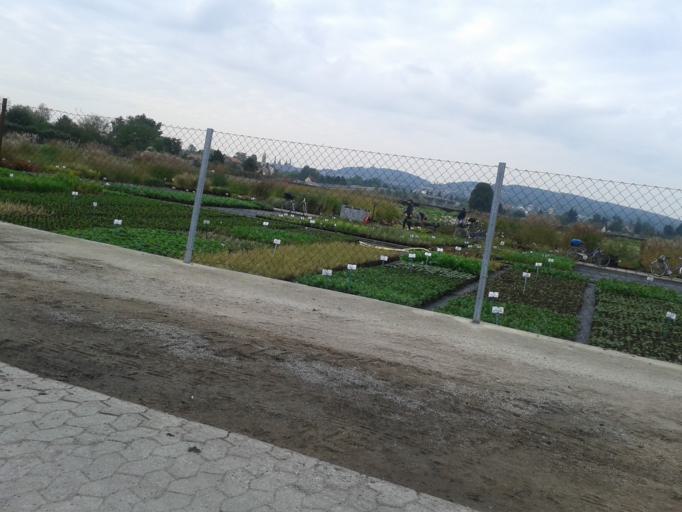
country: DE
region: Bavaria
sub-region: Upper Franconia
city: Bamberg
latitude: 49.9152
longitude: 10.8949
